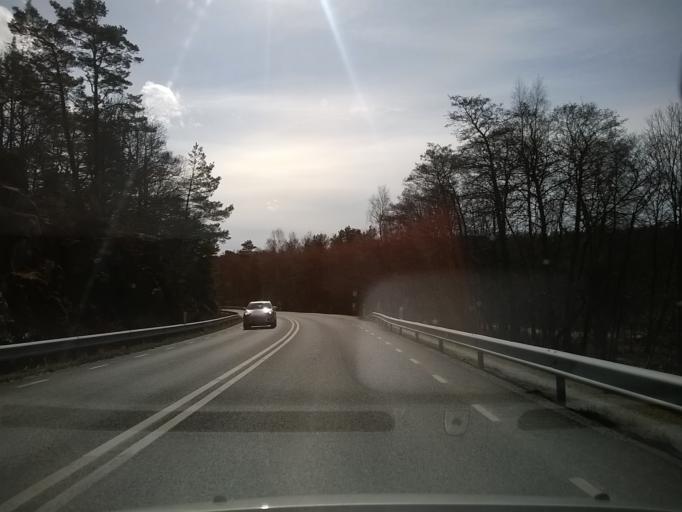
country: SE
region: Vaestra Goetaland
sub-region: Tjorns Kommun
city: Myggenas
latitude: 58.0823
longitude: 11.6948
